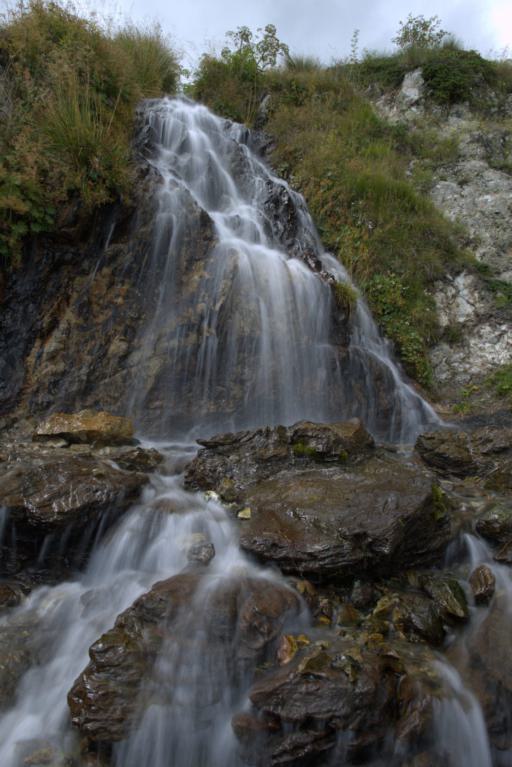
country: BG
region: Plovdiv
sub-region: Obshtina Karlovo
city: Karlovo
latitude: 42.7149
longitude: 24.8168
